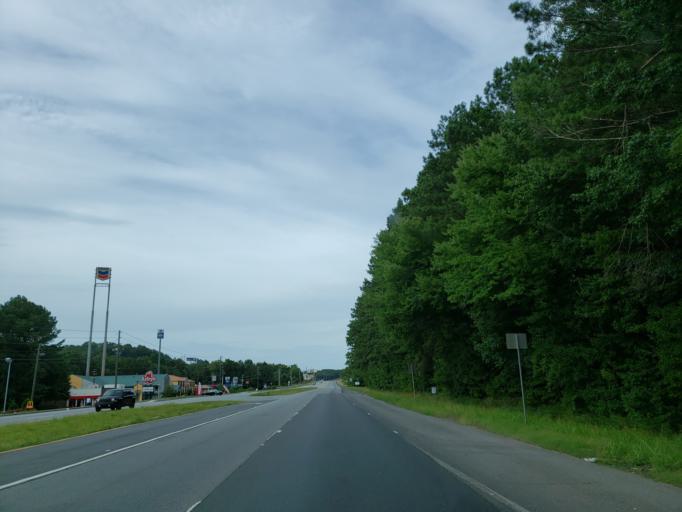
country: US
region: Georgia
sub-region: Bartow County
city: Cartersville
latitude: 34.2091
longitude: -84.7589
